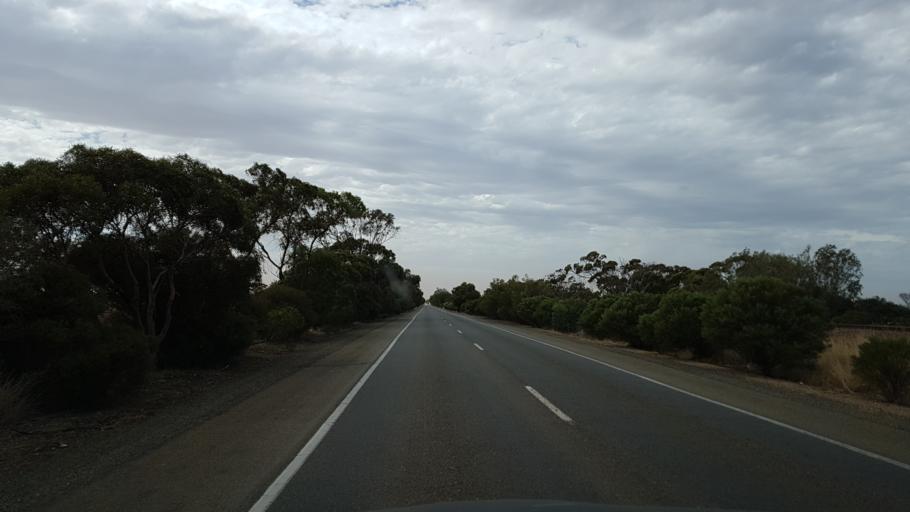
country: AU
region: South Australia
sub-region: Mallala
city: Mallala
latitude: -34.4317
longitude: 138.4970
